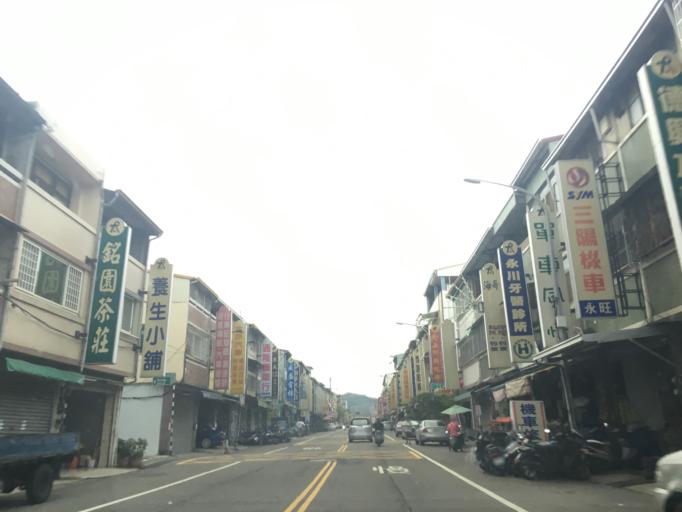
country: TW
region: Taiwan
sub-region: Taichung City
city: Taichung
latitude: 24.1523
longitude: 120.7333
